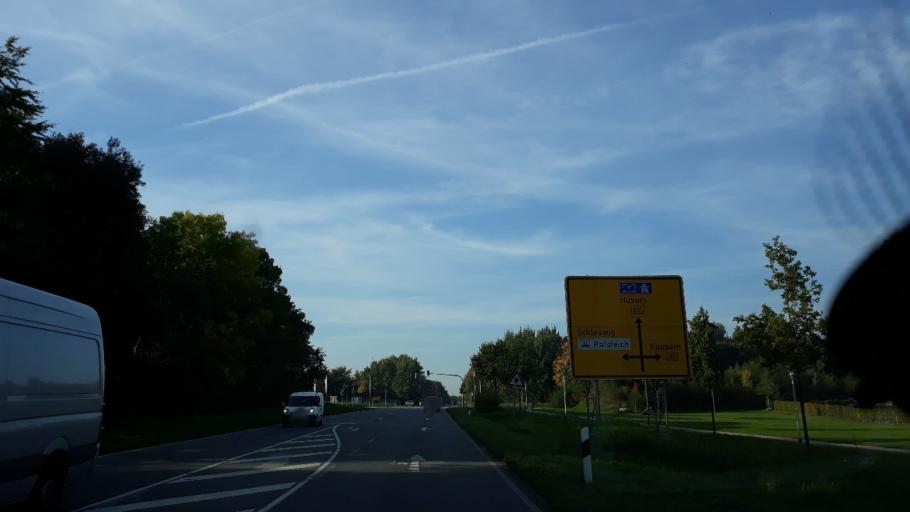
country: DE
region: Schleswig-Holstein
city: Schleswig
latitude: 54.5338
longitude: 9.5614
